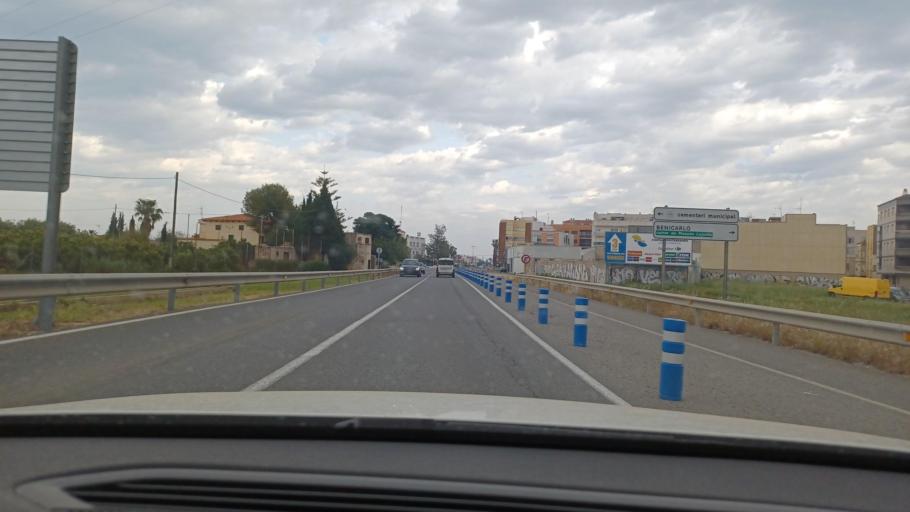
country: ES
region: Valencia
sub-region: Provincia de Castello
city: Benicarlo
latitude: 40.4244
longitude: 0.4205
